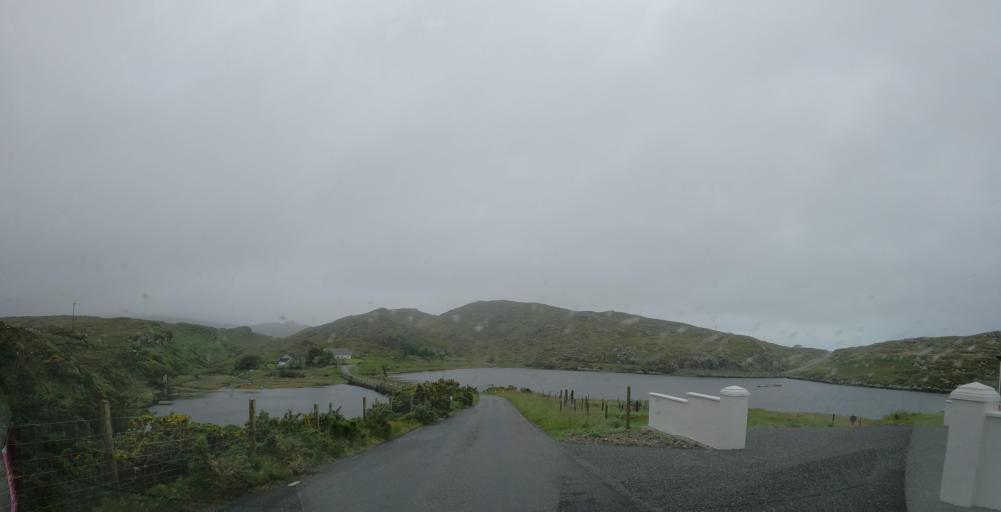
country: GB
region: Scotland
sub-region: Eilean Siar
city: Barra
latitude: 56.9901
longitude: -7.4179
